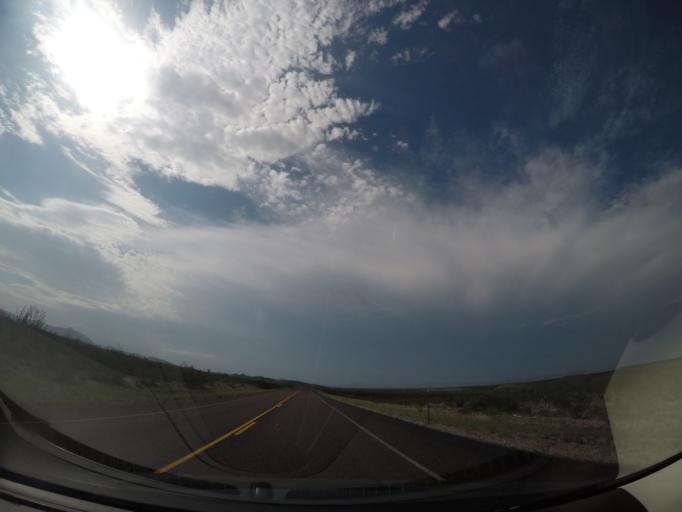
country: US
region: Texas
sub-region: Brewster County
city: Alpine
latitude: 29.7303
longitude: -103.1573
